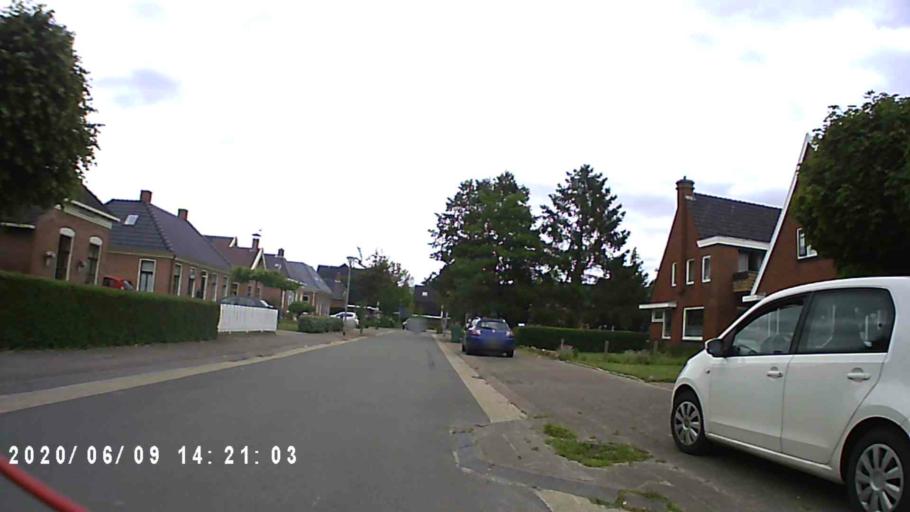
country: NL
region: Groningen
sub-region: Gemeente Bedum
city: Bedum
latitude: 53.2958
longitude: 6.5921
